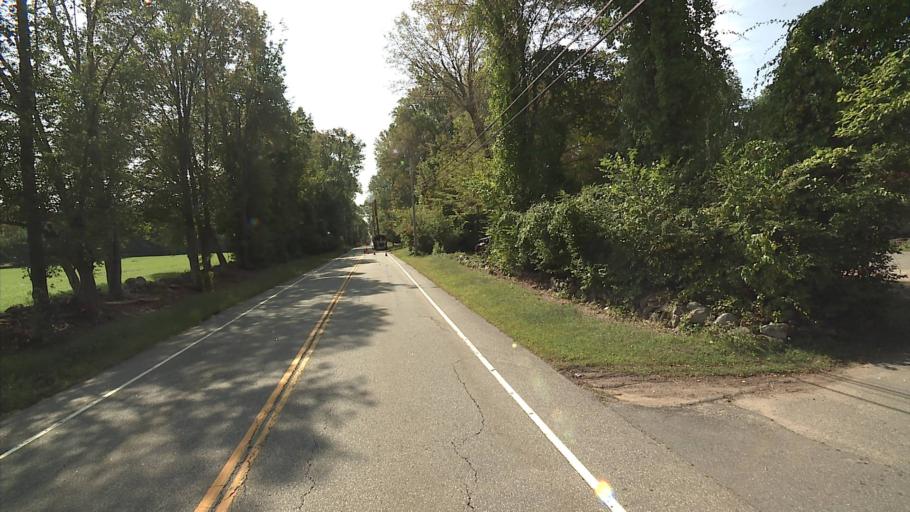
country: US
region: Connecticut
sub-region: Windham County
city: Putnam
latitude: 41.8513
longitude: -71.9590
